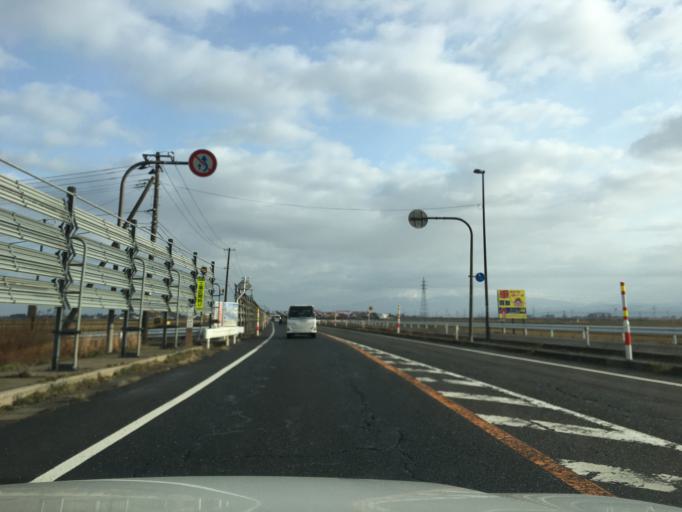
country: JP
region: Yamagata
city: Sakata
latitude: 38.8320
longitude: 139.8468
